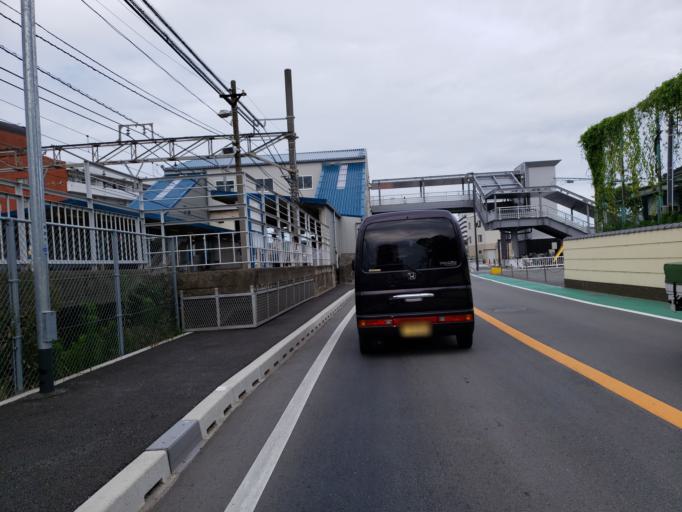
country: JP
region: Hyogo
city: Shirahamacho-usazakiminami
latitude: 34.7869
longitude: 134.7067
